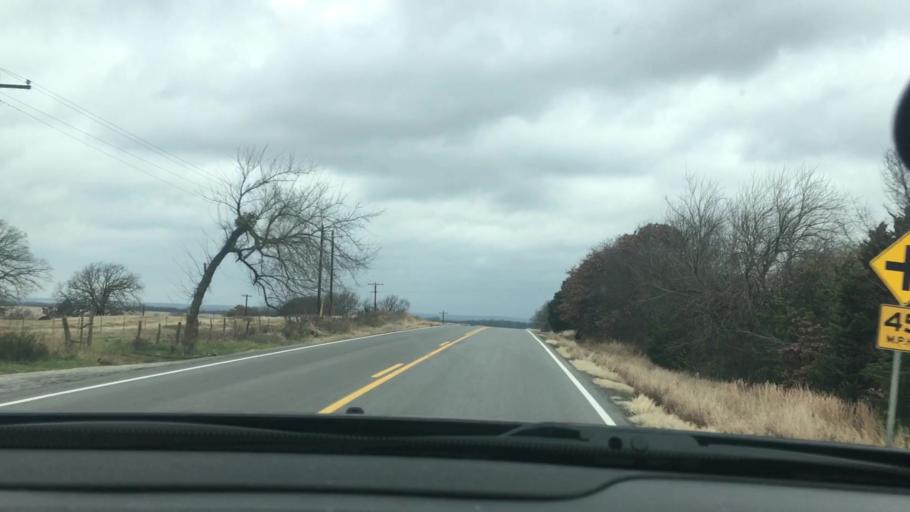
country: US
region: Oklahoma
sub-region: Atoka County
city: Atoka
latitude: 34.3749
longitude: -96.2480
